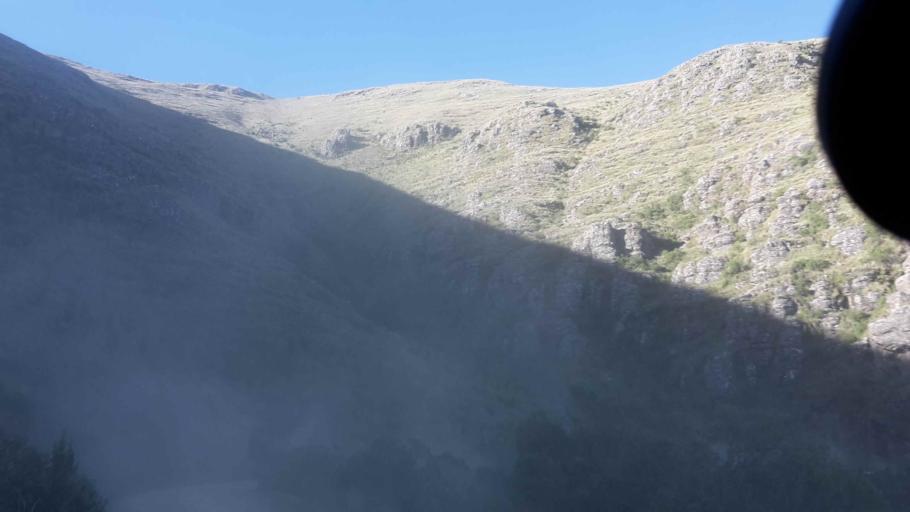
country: BO
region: Cochabamba
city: Arani
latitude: -17.7222
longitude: -65.6454
